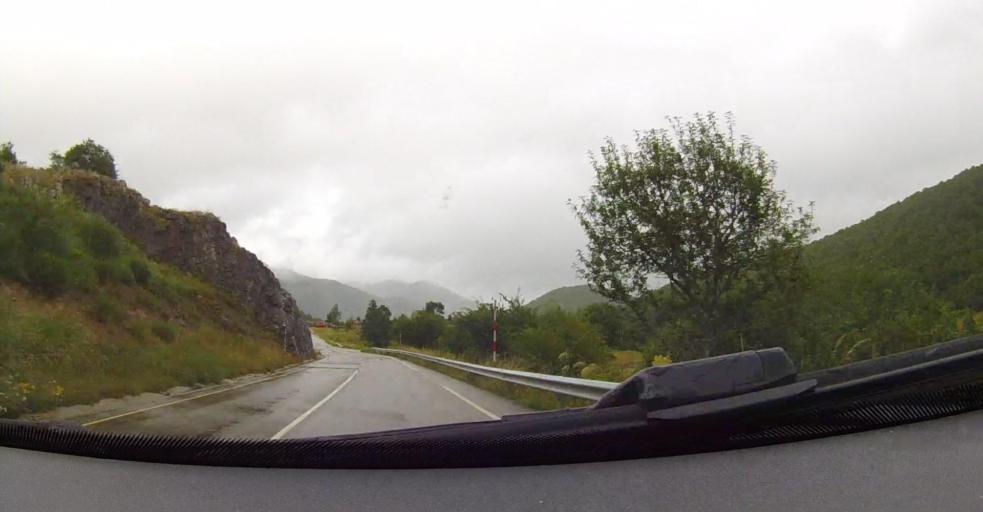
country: ES
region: Castille and Leon
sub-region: Provincia de Leon
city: Marana
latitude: 43.0696
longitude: -5.1730
